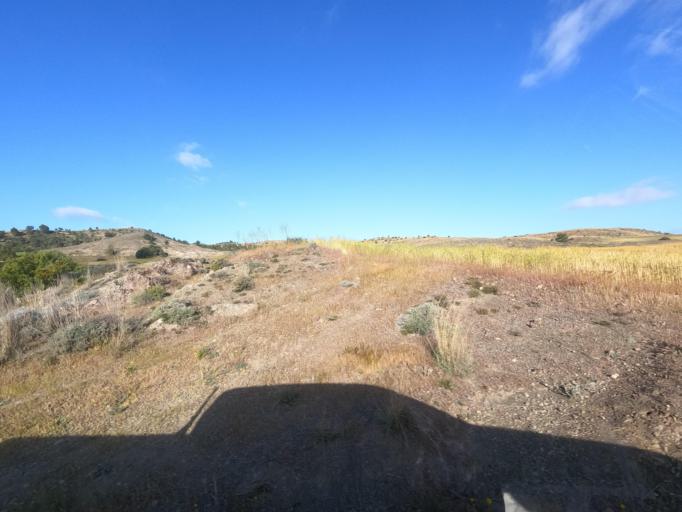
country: CY
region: Lefkosia
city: Peristerona
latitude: 35.0709
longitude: 33.0443
